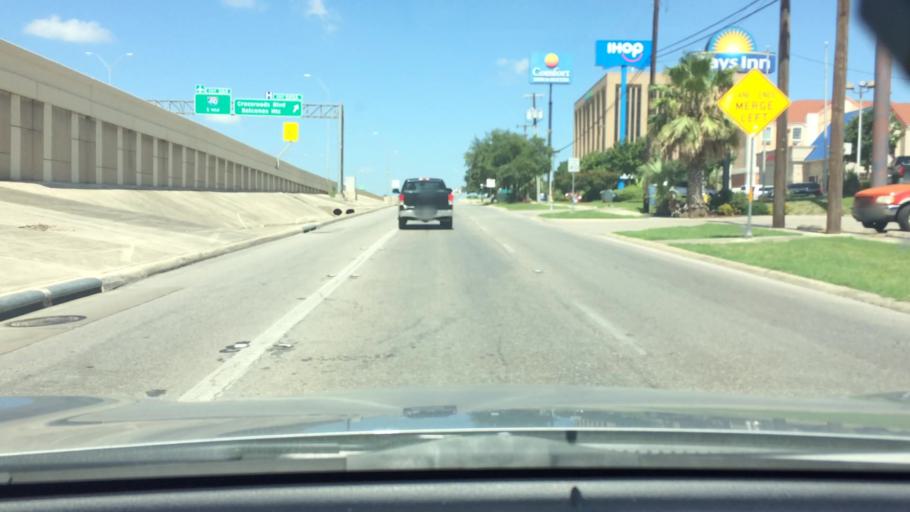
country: US
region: Texas
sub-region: Bexar County
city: Balcones Heights
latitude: 29.4851
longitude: -98.5354
